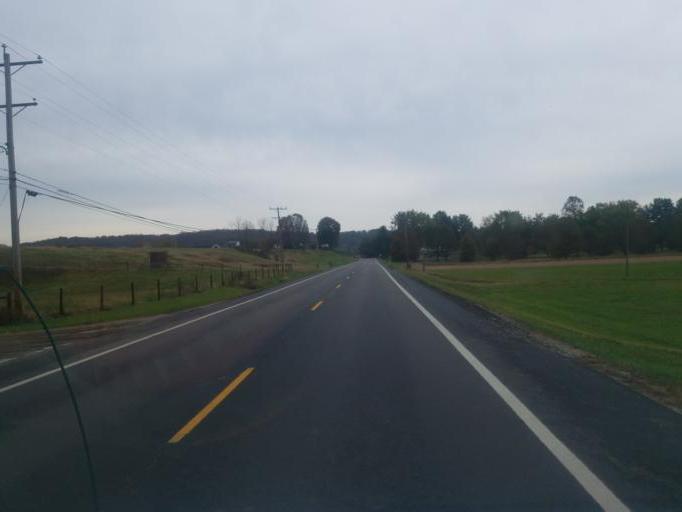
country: US
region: Ohio
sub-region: Washington County
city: Devola
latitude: 39.5312
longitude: -81.5276
